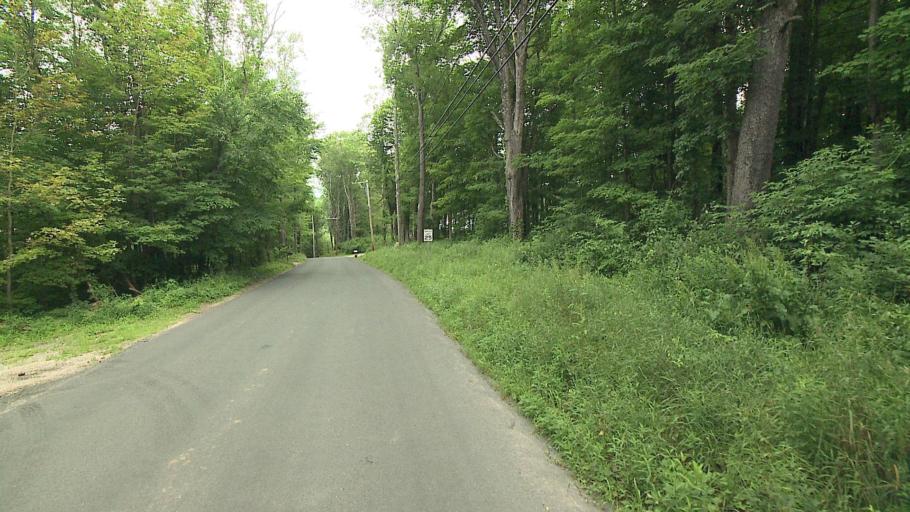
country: US
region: Connecticut
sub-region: Litchfield County
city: Winsted
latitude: 42.0031
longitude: -73.0034
